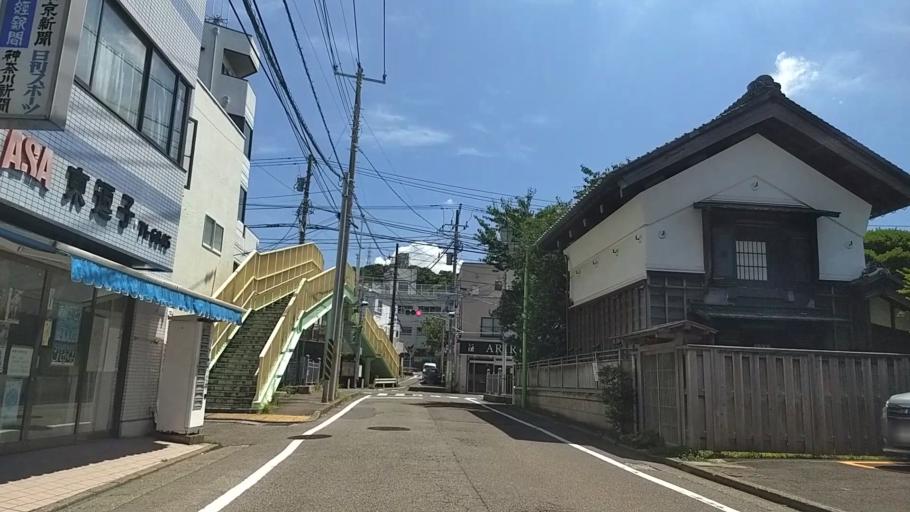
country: JP
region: Kanagawa
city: Zushi
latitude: 35.2981
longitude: 139.6009
